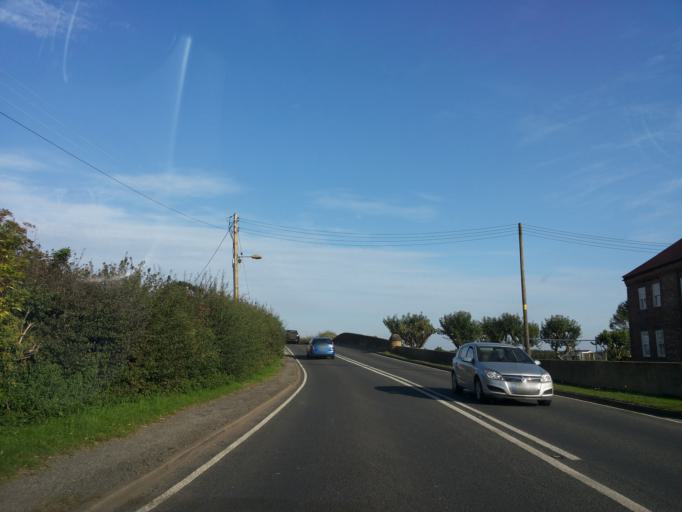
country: GB
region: England
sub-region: East Riding of Yorkshire
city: Snaith
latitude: 53.6853
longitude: -0.9907
